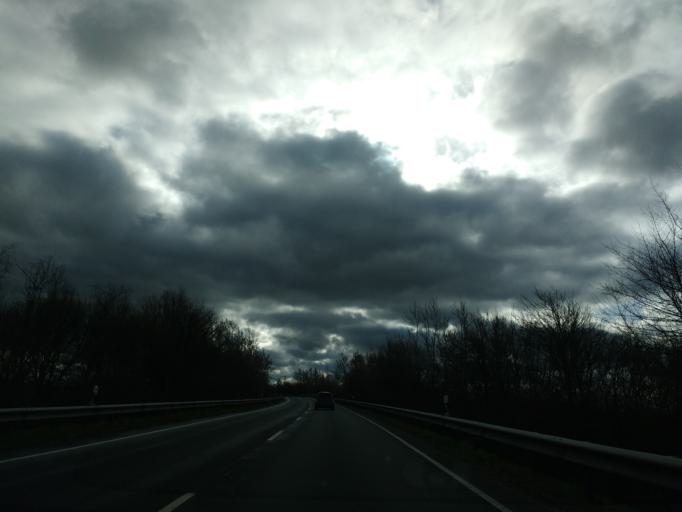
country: DE
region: Lower Saxony
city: Cuxhaven
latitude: 53.8262
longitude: 8.6810
